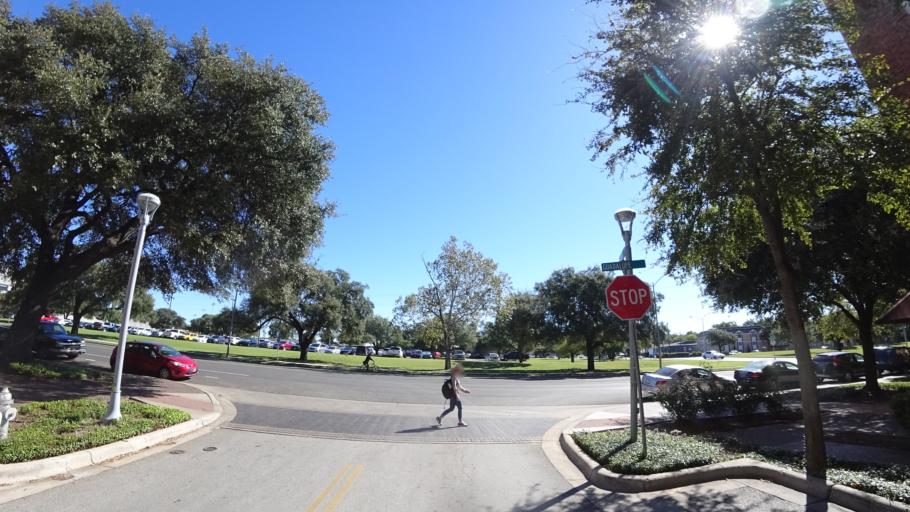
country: US
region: Texas
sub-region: Travis County
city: Austin
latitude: 30.3135
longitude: -97.7327
